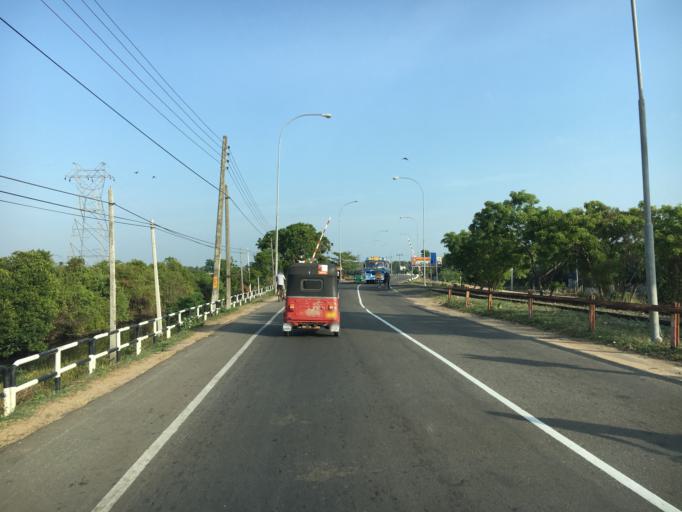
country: LK
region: Eastern Province
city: Eravur Town
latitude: 7.9192
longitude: 81.5174
